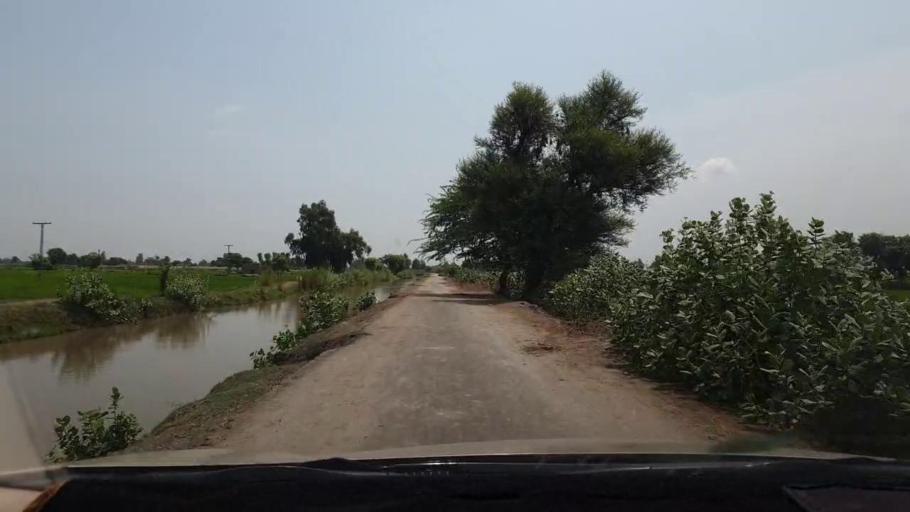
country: PK
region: Sindh
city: Naudero
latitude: 27.6590
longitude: 68.3284
